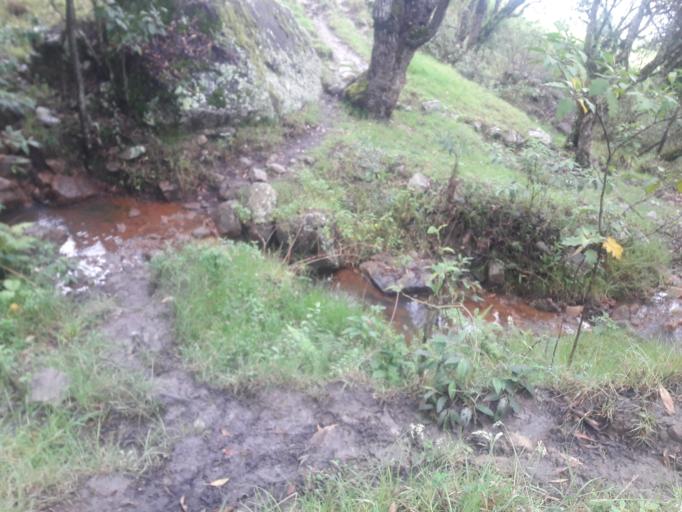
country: CO
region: Boyaca
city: Susacon
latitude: 6.1682
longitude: -72.6765
